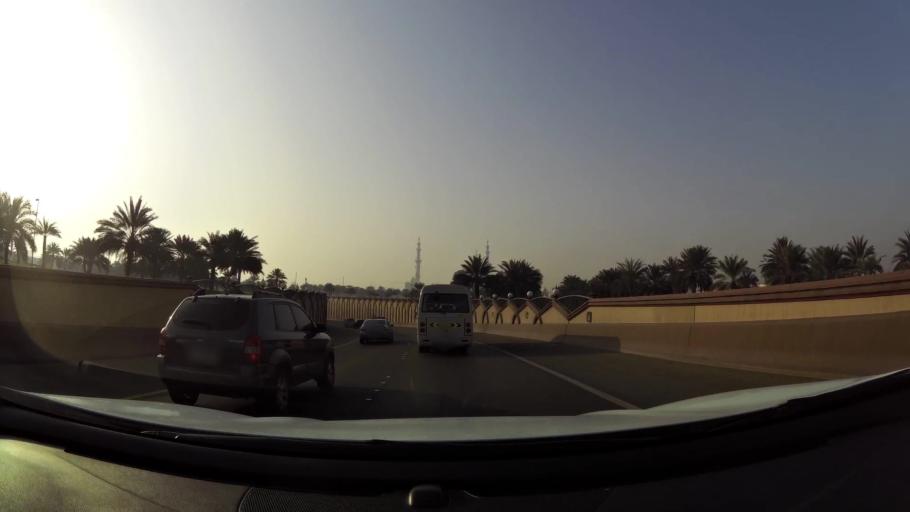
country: AE
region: Abu Dhabi
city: Abu Dhabi
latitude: 24.4198
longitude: 54.4741
